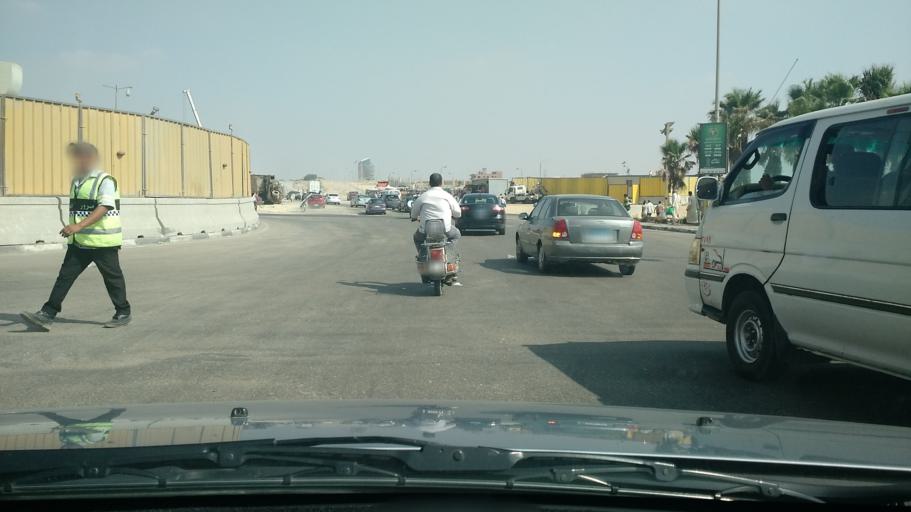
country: EG
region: Al Jizah
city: Awsim
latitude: 30.0083
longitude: 30.9824
